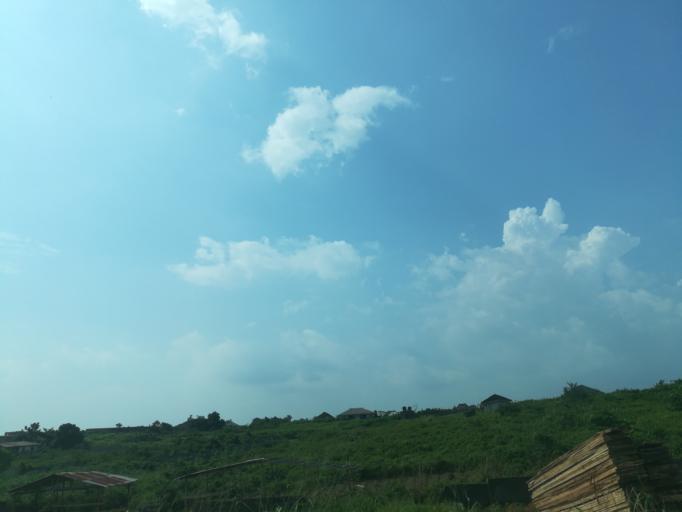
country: NG
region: Lagos
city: Ikorodu
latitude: 6.6193
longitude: 3.6542
